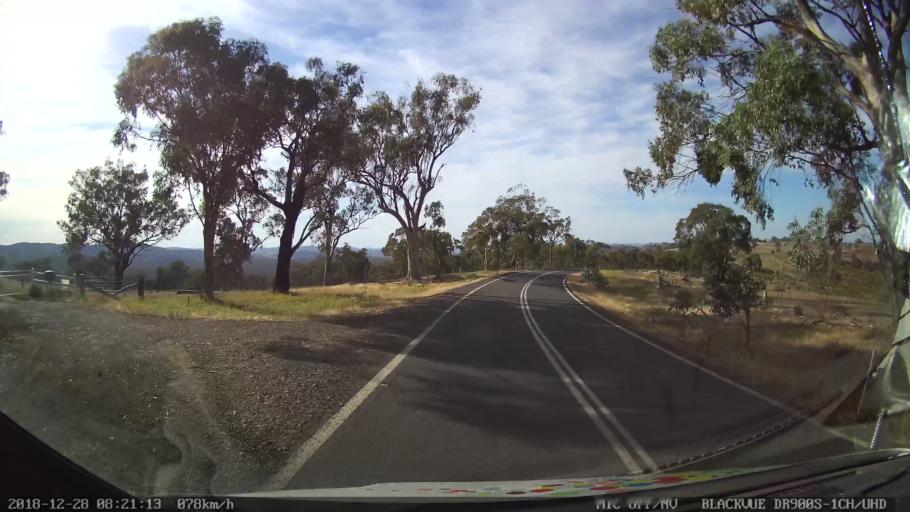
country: AU
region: New South Wales
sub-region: Blayney
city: Blayney
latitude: -33.8801
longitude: 149.3506
